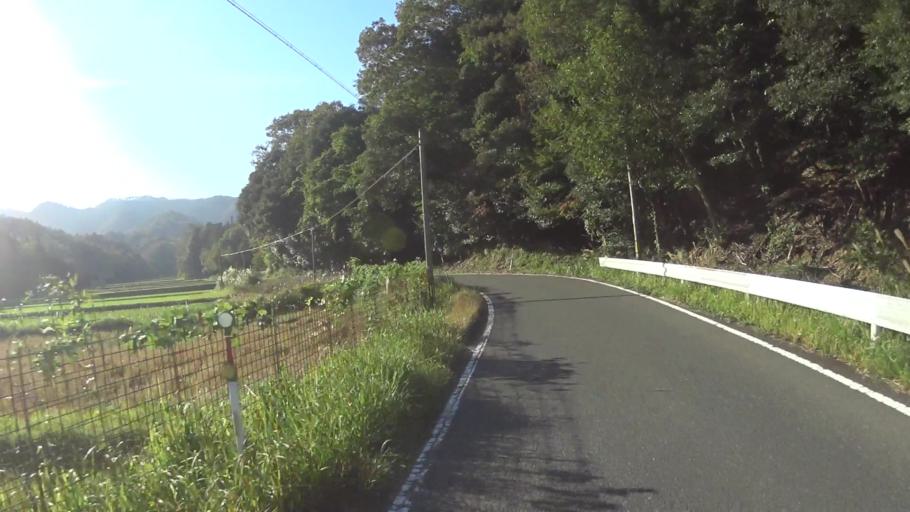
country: JP
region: Hyogo
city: Toyooka
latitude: 35.6105
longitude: 134.8869
